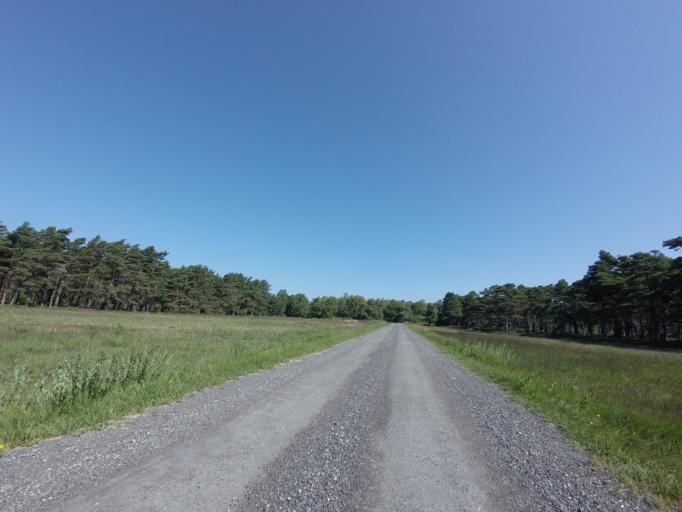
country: SE
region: Skane
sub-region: Vellinge Kommun
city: Ljunghusen
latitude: 55.4062
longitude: 12.8877
